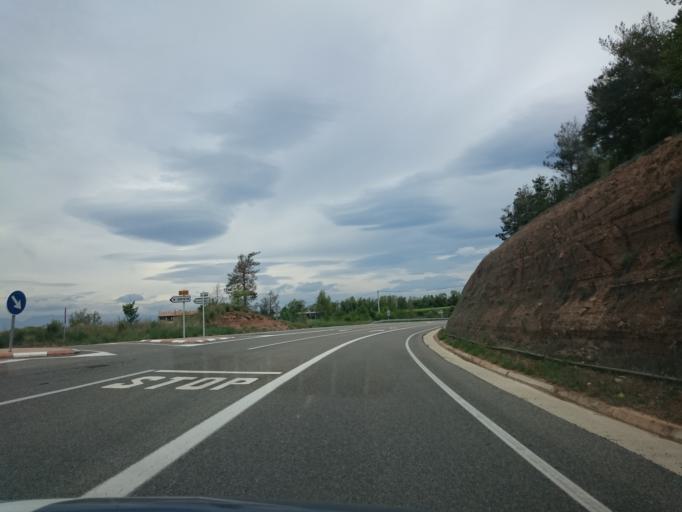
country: ES
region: Catalonia
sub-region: Provincia de Barcelona
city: Olost
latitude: 41.9619
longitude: 2.1288
